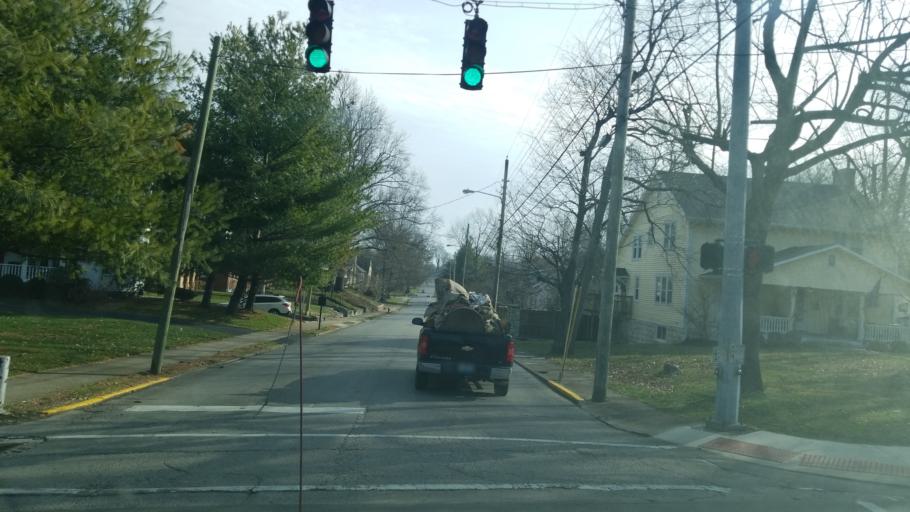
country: US
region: Kentucky
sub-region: Boyle County
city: Danville
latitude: 37.6498
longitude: -84.7827
